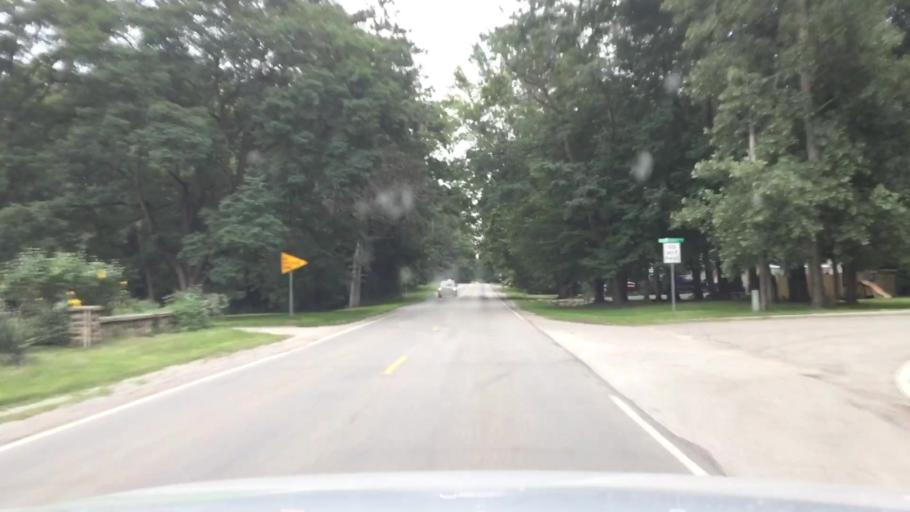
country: US
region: Michigan
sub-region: Genesee County
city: Argentine
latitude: 42.8098
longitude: -83.8888
